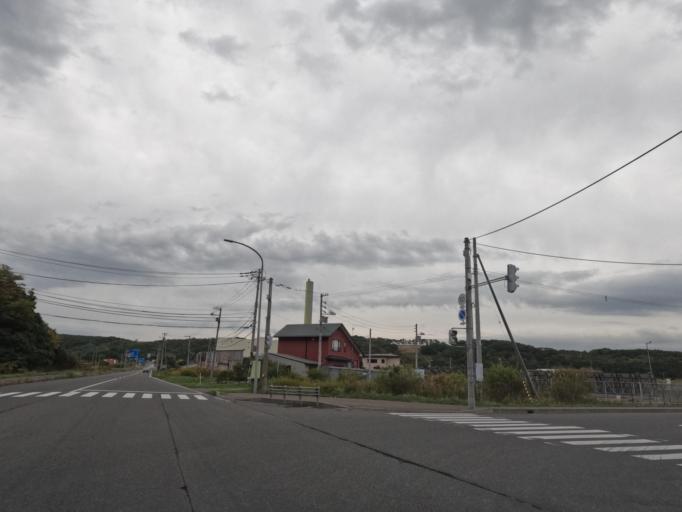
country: JP
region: Hokkaido
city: Date
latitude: 42.3838
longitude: 140.9122
